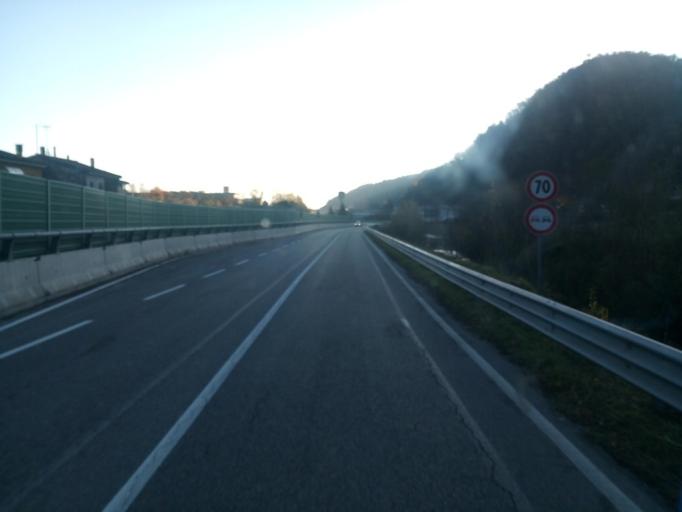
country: IT
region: Veneto
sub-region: Provincia di Vicenza
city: Torrebelvicino
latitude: 45.7144
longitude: 11.3123
